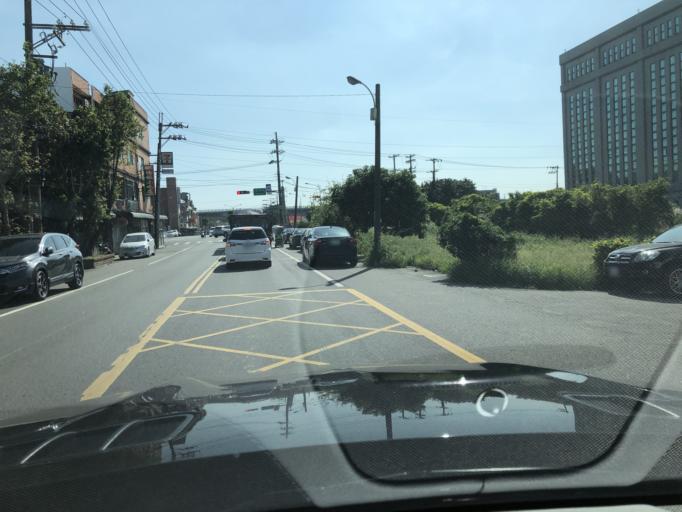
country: TW
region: Taiwan
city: Taoyuan City
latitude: 25.0838
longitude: 121.2859
